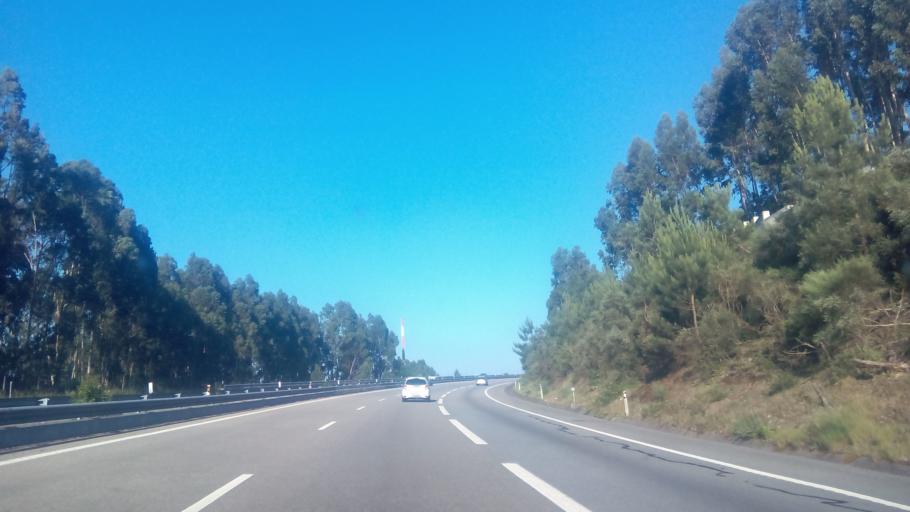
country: PT
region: Porto
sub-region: Pacos de Ferreira
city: Pacos de Ferreira
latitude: 41.2648
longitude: -8.3815
